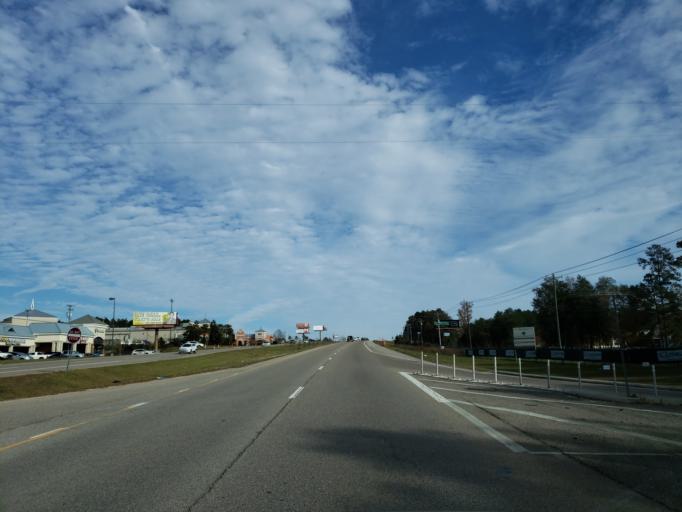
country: US
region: Mississippi
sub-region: Lamar County
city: West Hattiesburg
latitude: 31.3171
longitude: -89.4218
